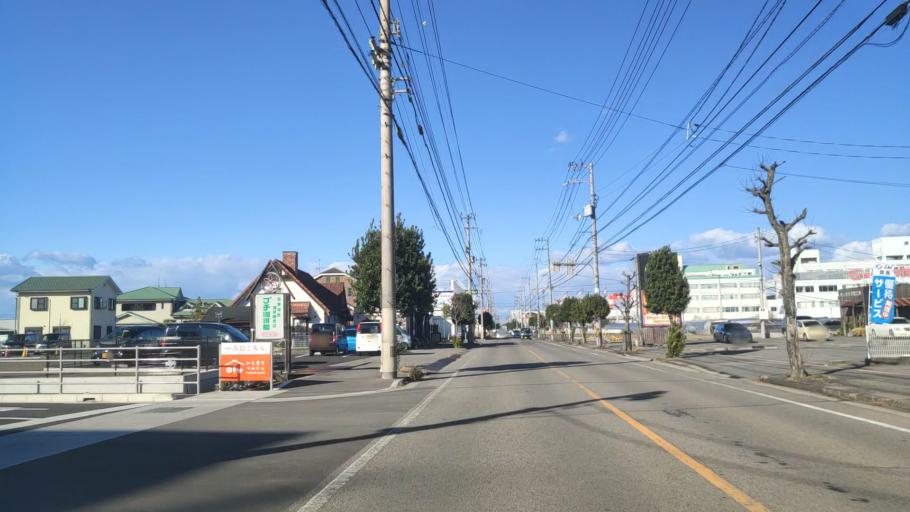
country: JP
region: Ehime
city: Saijo
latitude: 33.9265
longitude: 133.1907
